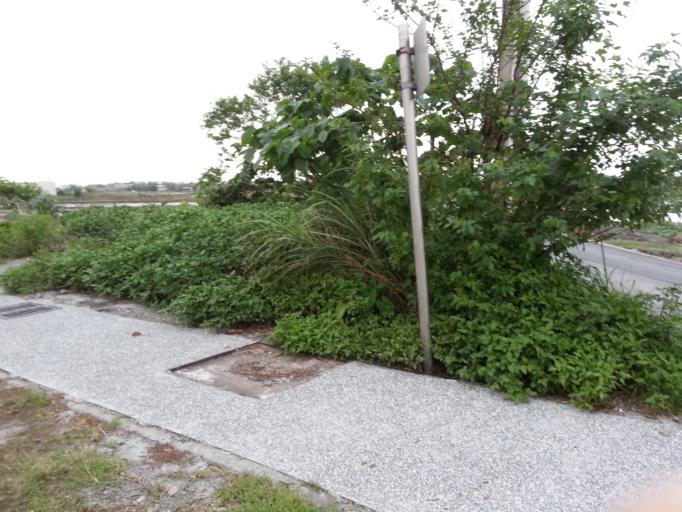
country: TW
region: Taiwan
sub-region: Yilan
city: Yilan
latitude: 24.6195
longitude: 121.8435
